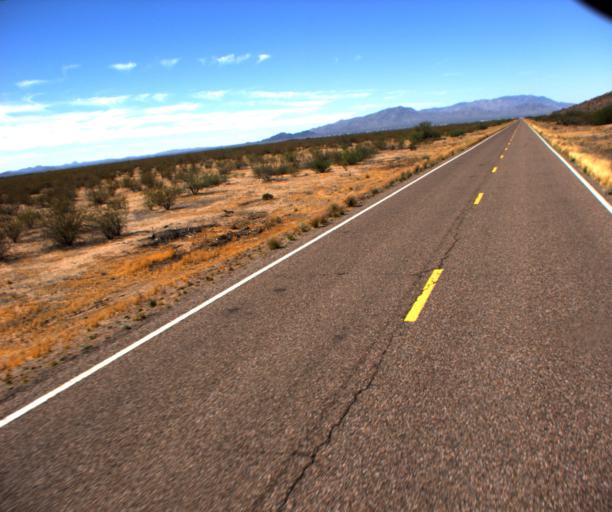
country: US
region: Arizona
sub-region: Yavapai County
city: Congress
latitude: 34.0184
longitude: -113.0987
